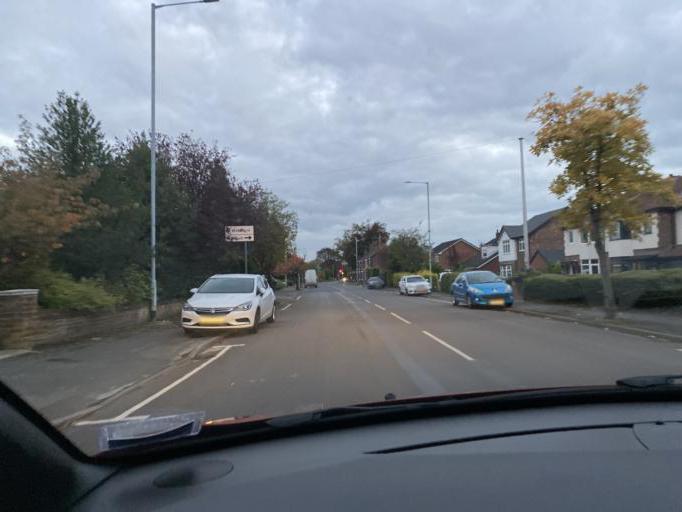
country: GB
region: England
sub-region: Borough of Stockport
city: Hazel Grove
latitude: 53.3696
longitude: -2.1244
